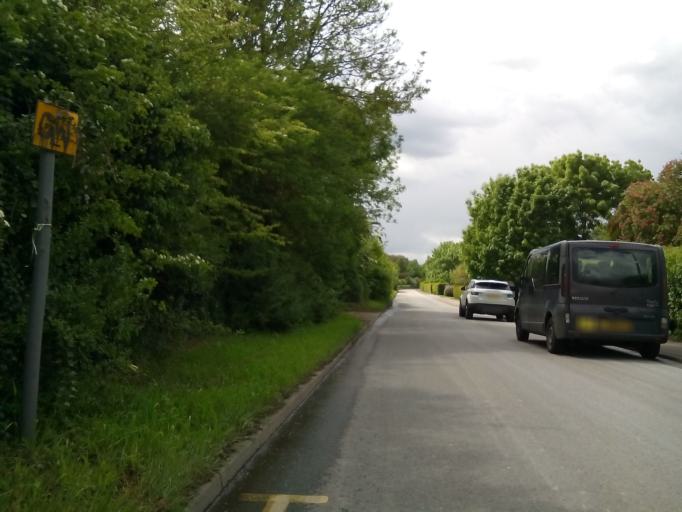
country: GB
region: England
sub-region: Cambridgeshire
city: Fulbourn
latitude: 52.1848
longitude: 0.2019
